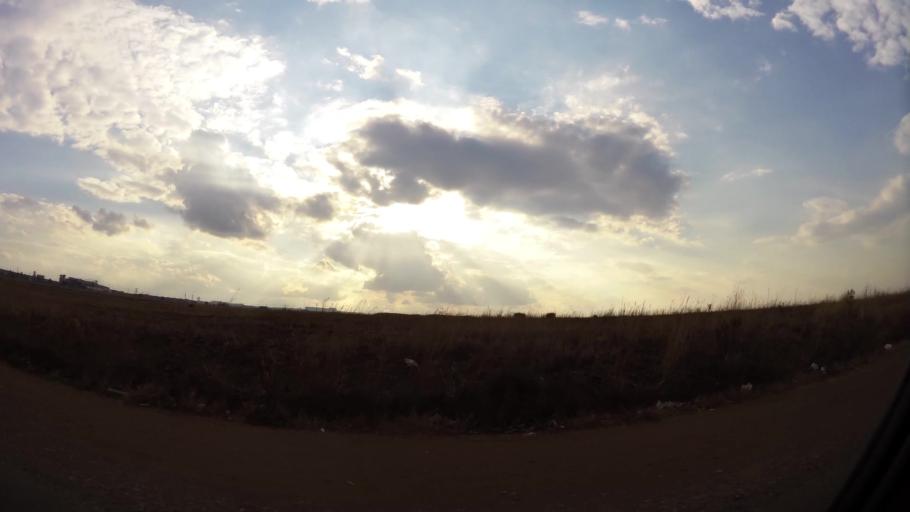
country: ZA
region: Gauteng
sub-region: Sedibeng District Municipality
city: Vereeniging
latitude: -26.6576
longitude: 27.8694
